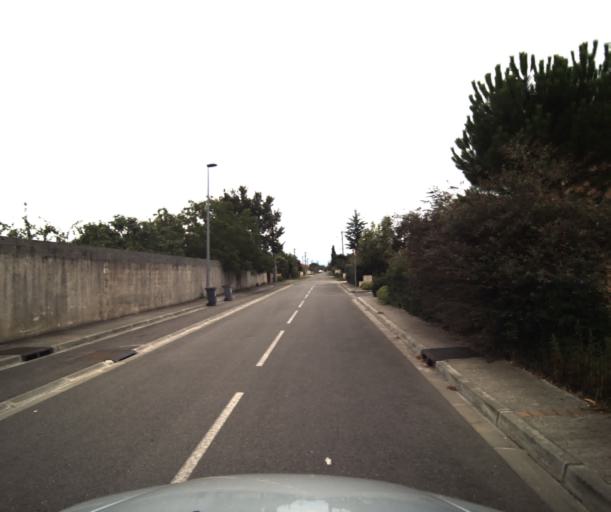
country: FR
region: Midi-Pyrenees
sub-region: Departement de la Haute-Garonne
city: Muret
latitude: 43.4543
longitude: 1.3178
